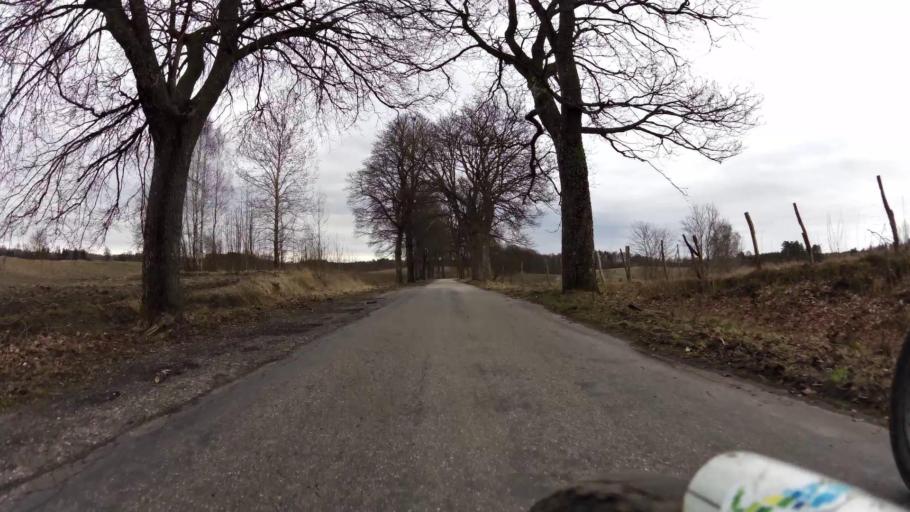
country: PL
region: Pomeranian Voivodeship
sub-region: Powiat bytowski
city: Trzebielino
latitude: 54.1024
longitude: 17.1302
